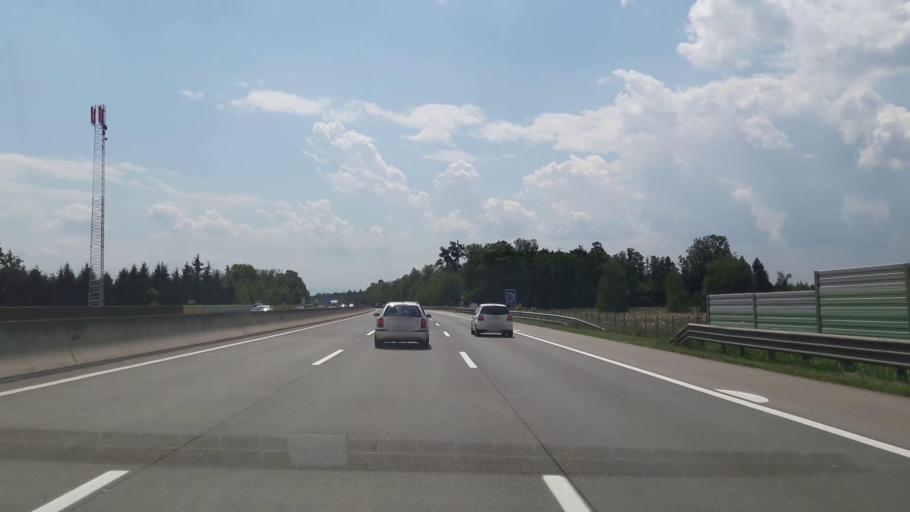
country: AT
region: Upper Austria
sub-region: Politischer Bezirk Linz-Land
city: Horsching
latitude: 48.1733
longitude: 14.1744
